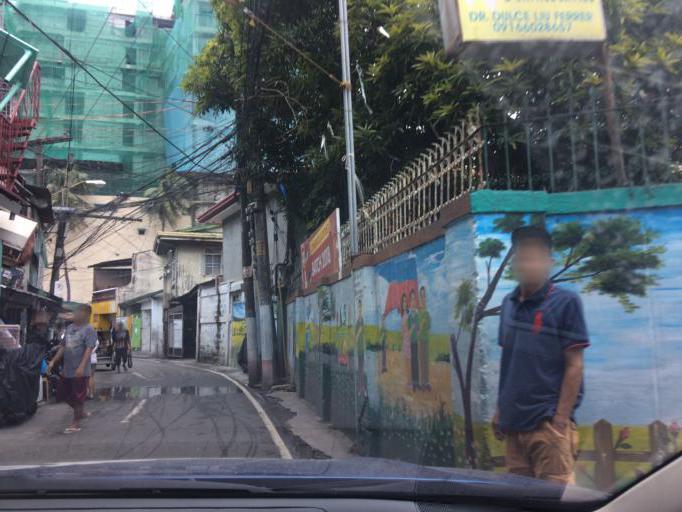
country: PH
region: Metro Manila
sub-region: Makati City
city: Makati City
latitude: 14.5365
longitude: 121.0019
